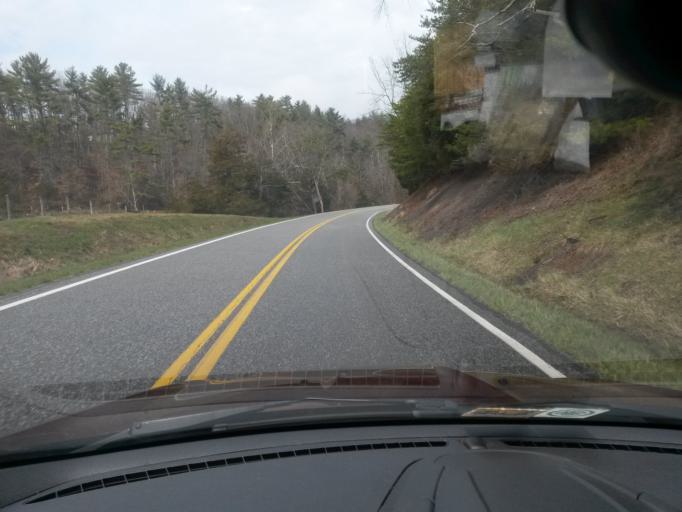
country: US
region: Virginia
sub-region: Bath County
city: Warm Springs
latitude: 38.0076
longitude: -79.6405
